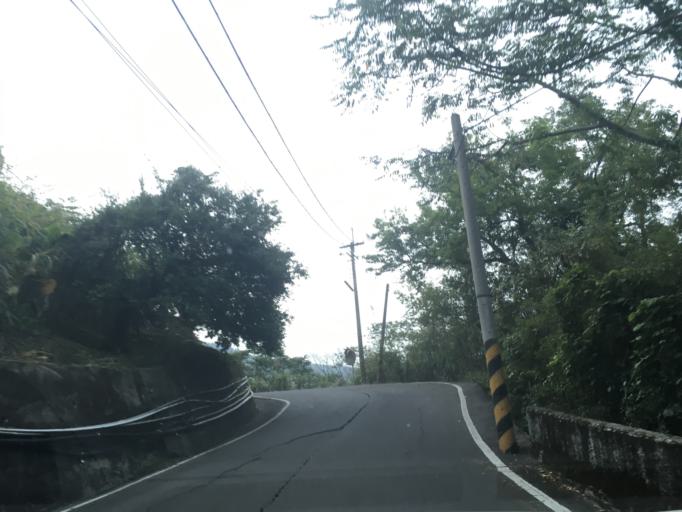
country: TW
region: Taiwan
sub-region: Nantou
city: Puli
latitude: 23.9473
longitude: 120.8537
